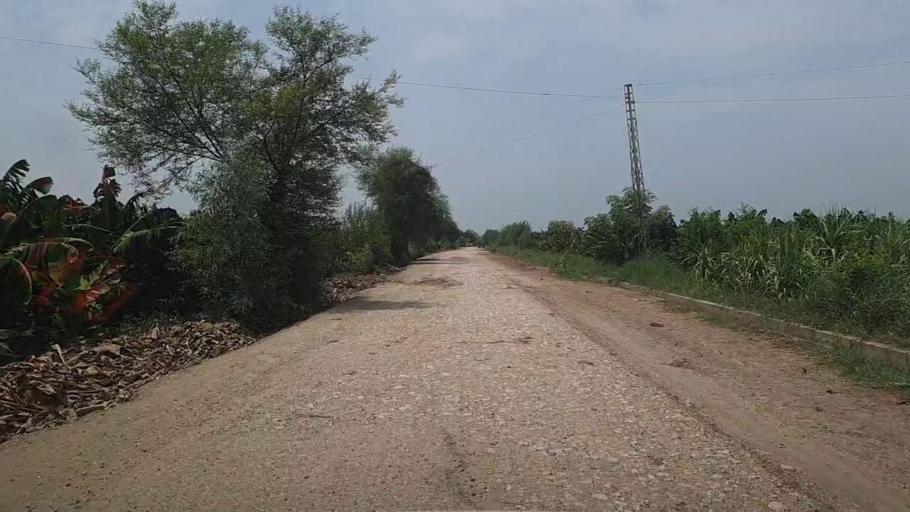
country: PK
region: Sindh
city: Karaundi
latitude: 26.9171
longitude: 68.3356
